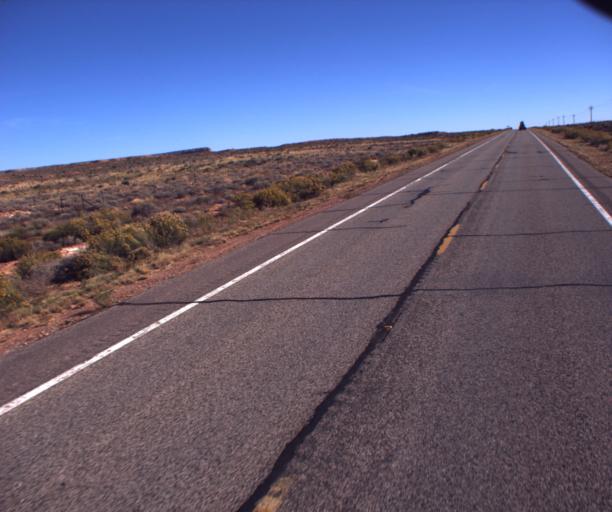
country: US
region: Arizona
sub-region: Coconino County
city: Fredonia
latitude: 36.8696
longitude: -112.6855
